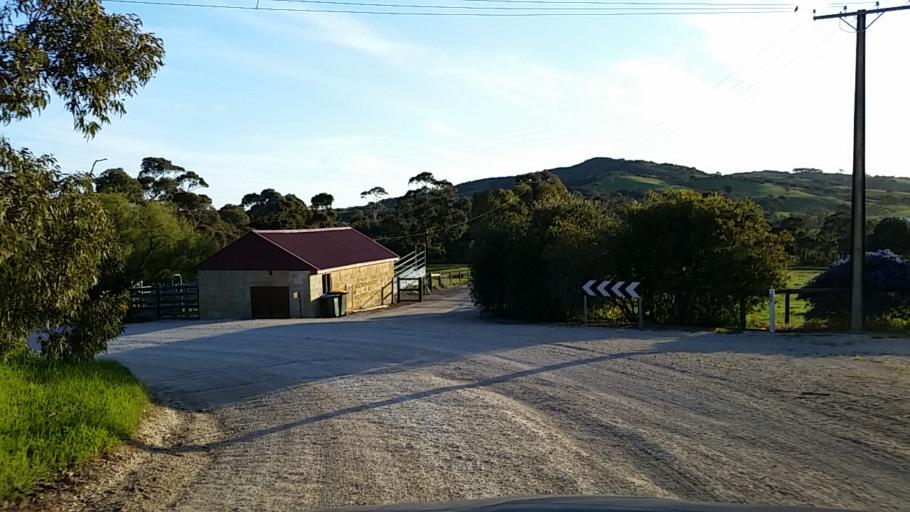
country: AU
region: South Australia
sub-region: Alexandrina
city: Mount Compass
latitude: -35.3145
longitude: 138.6695
